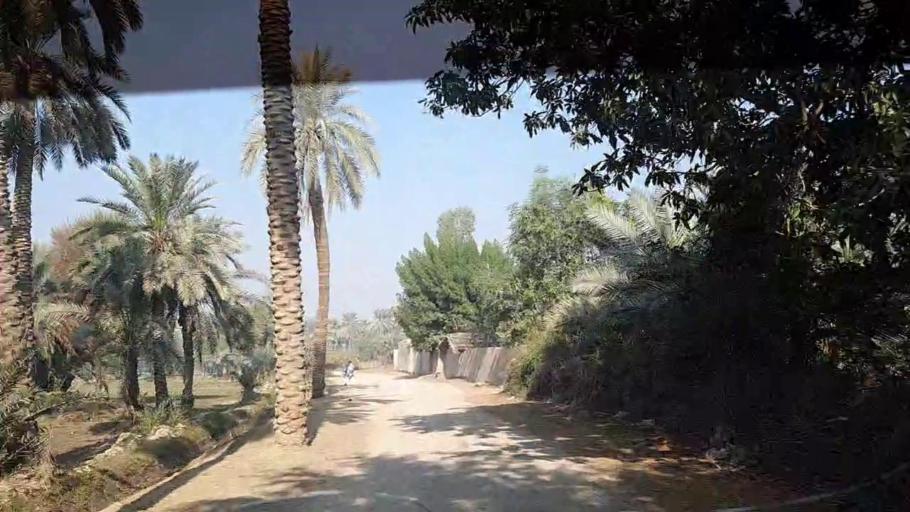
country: PK
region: Sindh
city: Khairpur
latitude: 27.4932
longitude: 68.7391
